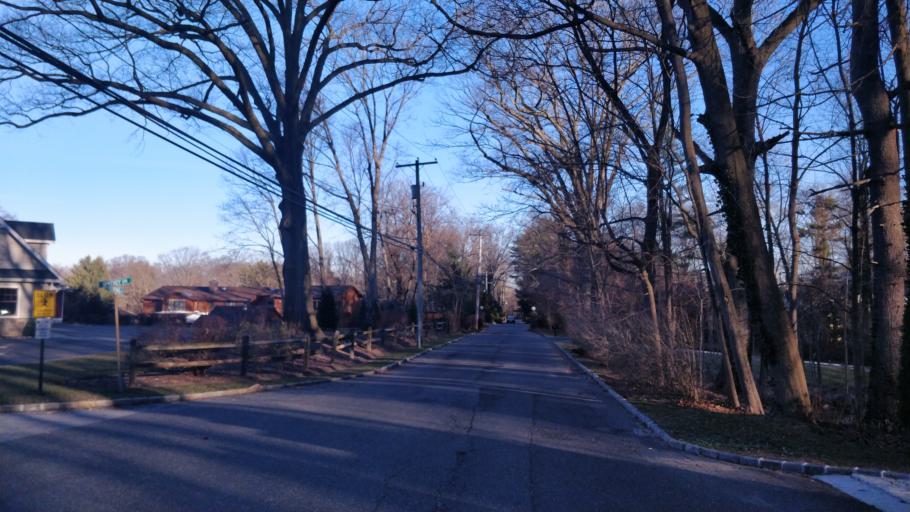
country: US
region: New York
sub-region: Nassau County
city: Glen Cove
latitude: 40.8744
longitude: -73.6489
